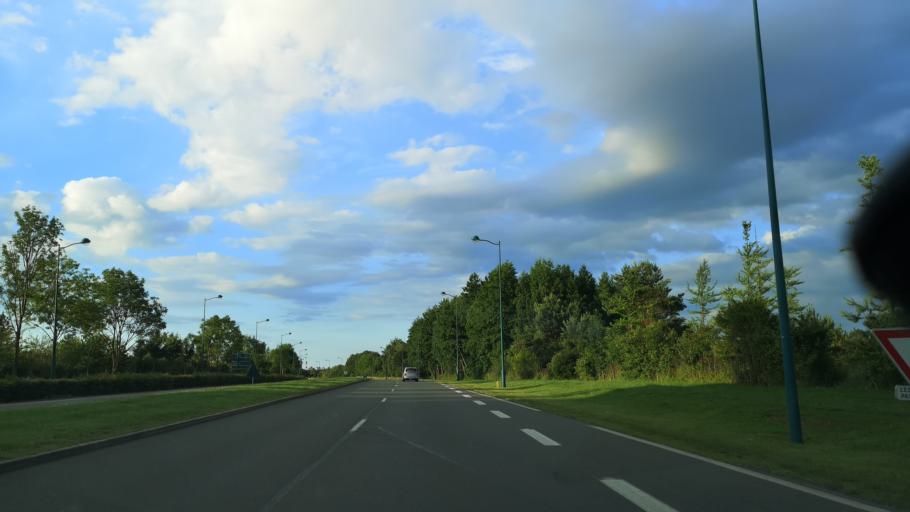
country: FR
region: Ile-de-France
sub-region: Departement de Seine-et-Marne
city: Magny-le-Hongre
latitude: 48.8561
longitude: 2.8028
